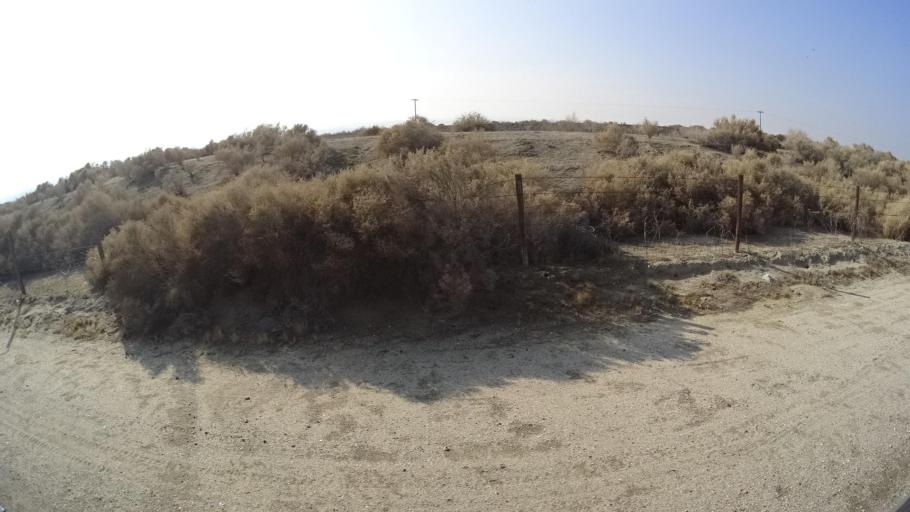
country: US
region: California
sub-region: Kern County
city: Buttonwillow
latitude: 35.3098
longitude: -119.3757
